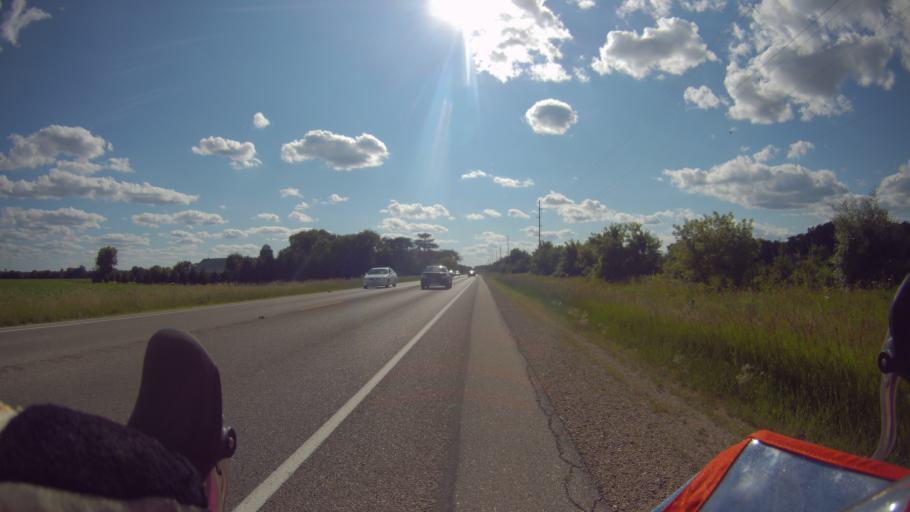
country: US
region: Wisconsin
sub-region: Dane County
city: Stoughton
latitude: 42.9190
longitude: -89.2968
